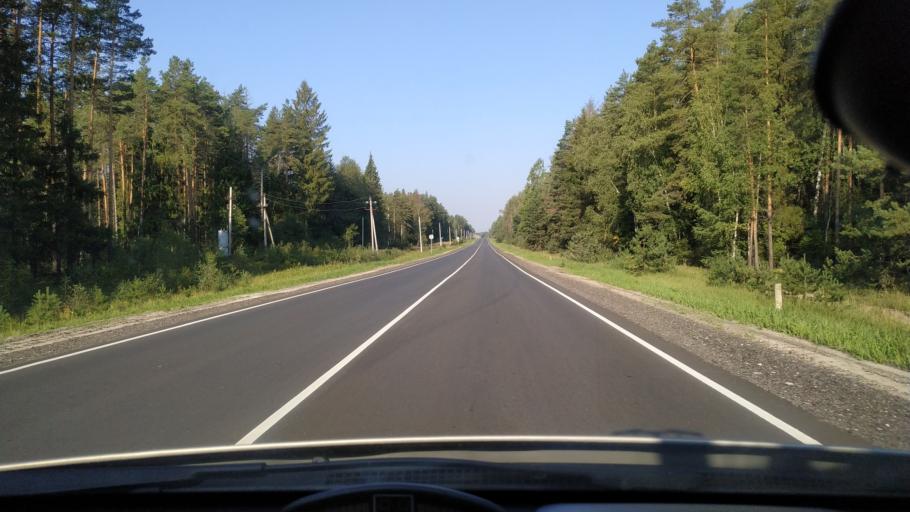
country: RU
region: Moskovskaya
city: Roshal'
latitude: 55.6573
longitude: 39.7957
